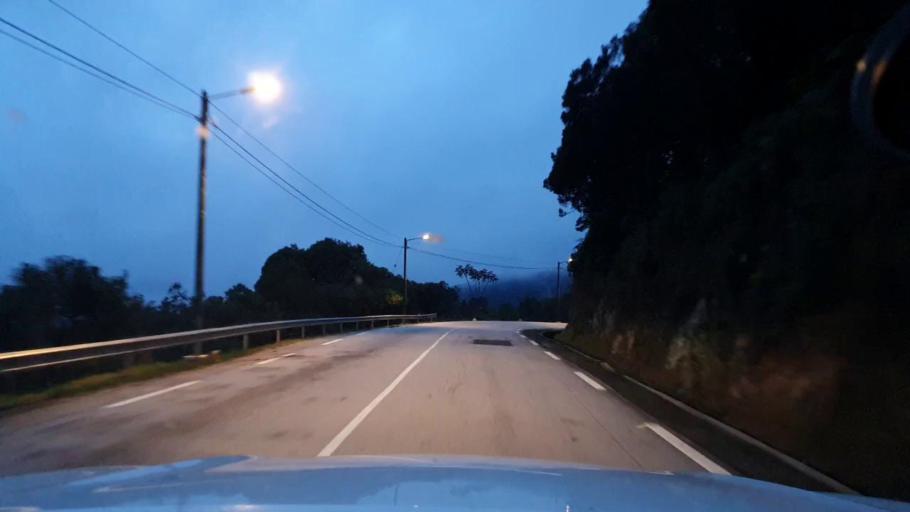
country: RW
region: Southern Province
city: Nzega
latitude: -2.5254
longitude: 29.3794
